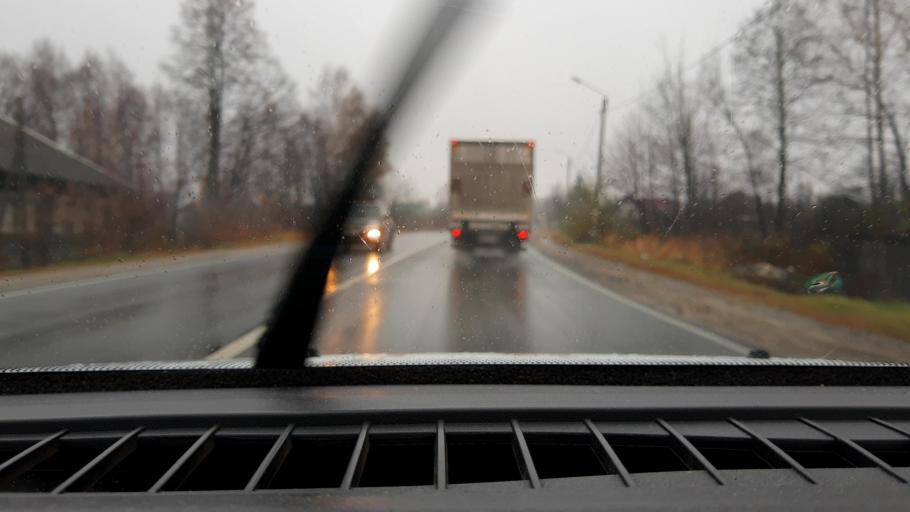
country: RU
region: Nizjnij Novgorod
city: Linda
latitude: 56.5676
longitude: 44.0249
